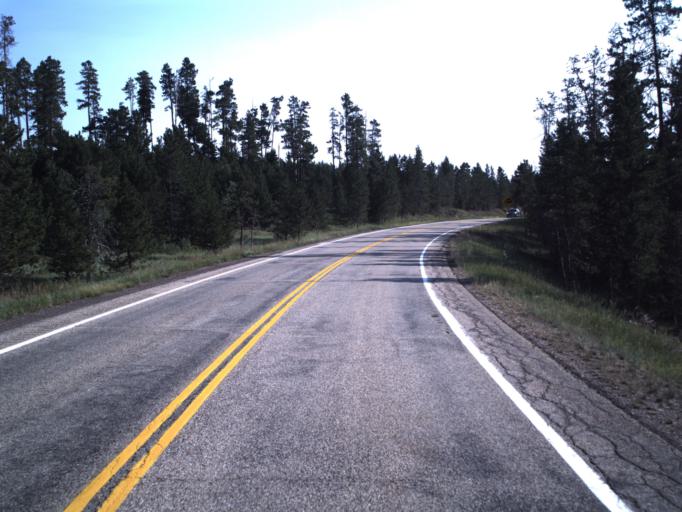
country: US
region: Utah
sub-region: Daggett County
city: Manila
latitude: 40.8463
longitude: -109.4653
